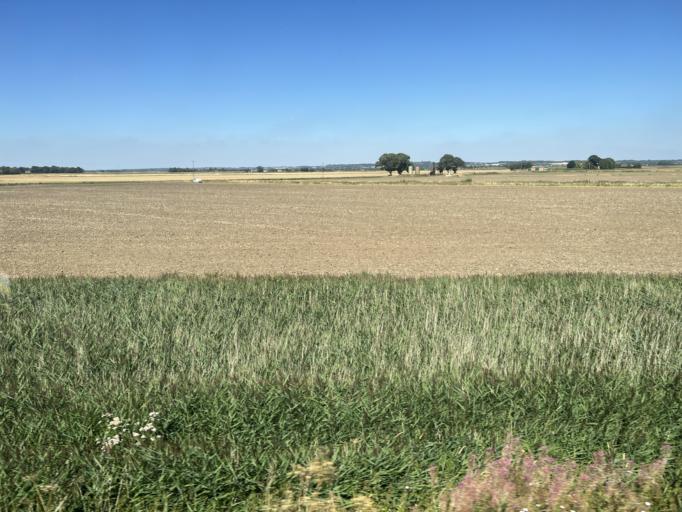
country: GB
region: England
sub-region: Lincolnshire
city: Spilsby
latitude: 53.1111
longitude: 0.1245
